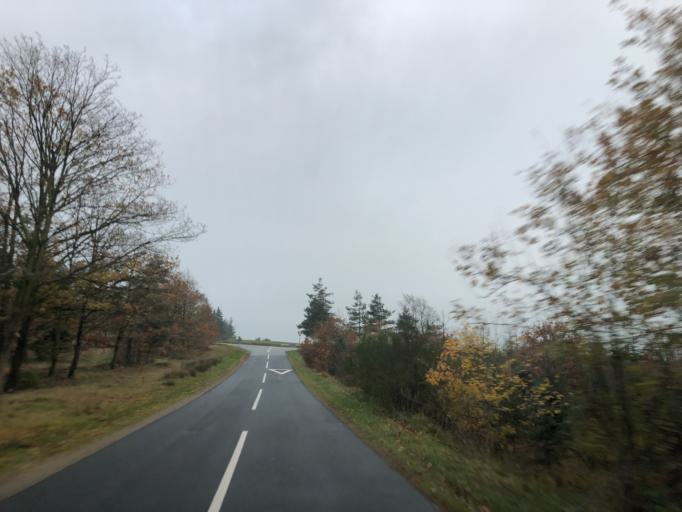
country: DK
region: Central Jutland
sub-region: Ringkobing-Skjern Kommune
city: Videbaek
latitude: 56.1858
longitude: 8.6433
